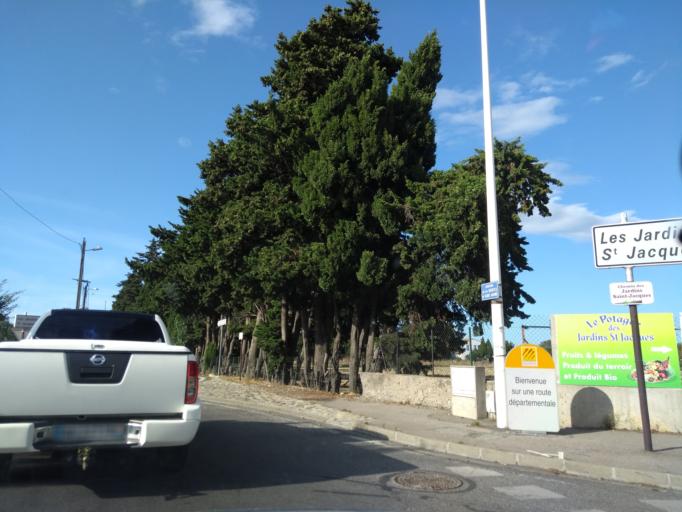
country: FR
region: Languedoc-Roussillon
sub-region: Departement des Pyrenees-Orientales
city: Perpignan
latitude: 42.7028
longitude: 2.9097
